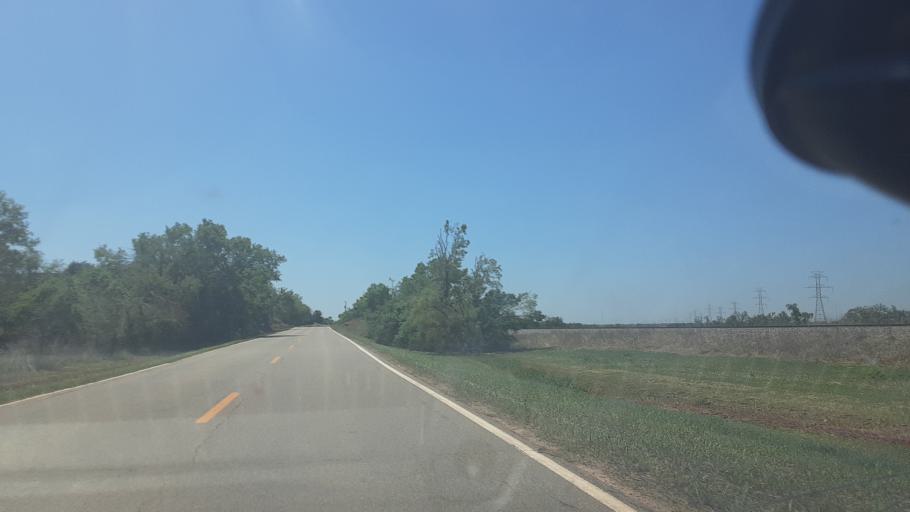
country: US
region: Oklahoma
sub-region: Logan County
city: Langston
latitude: 36.0919
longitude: -97.3957
